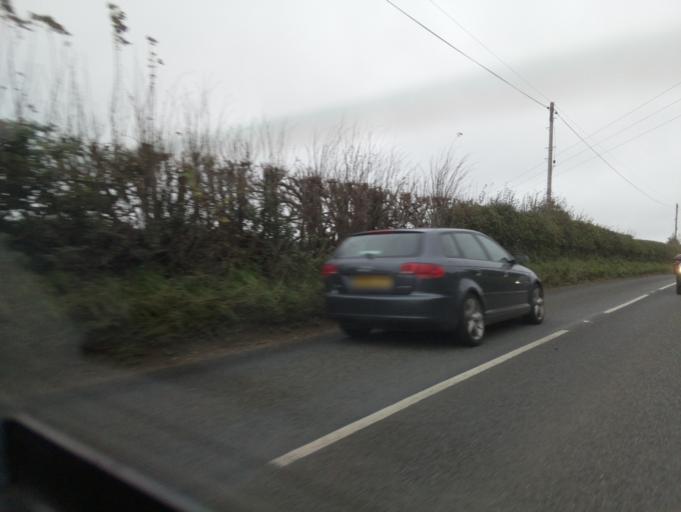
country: GB
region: England
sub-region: Dorset
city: Sherborne
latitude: 50.9578
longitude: -2.5399
